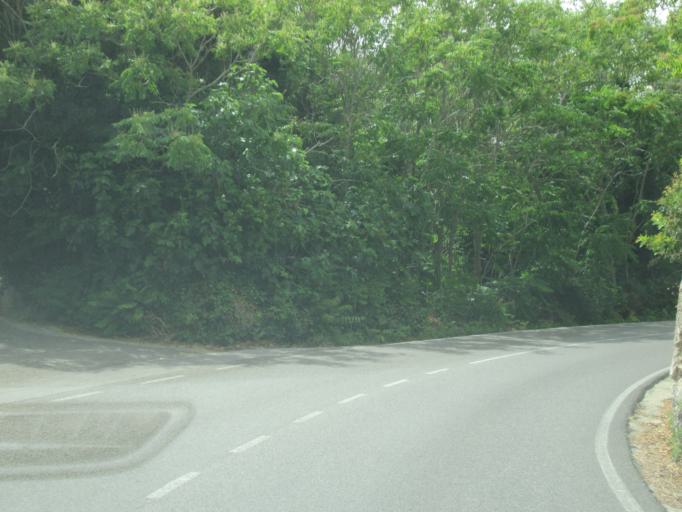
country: ES
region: Balearic Islands
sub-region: Illes Balears
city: Es Migjorn Gran
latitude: 39.9457
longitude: 4.0453
